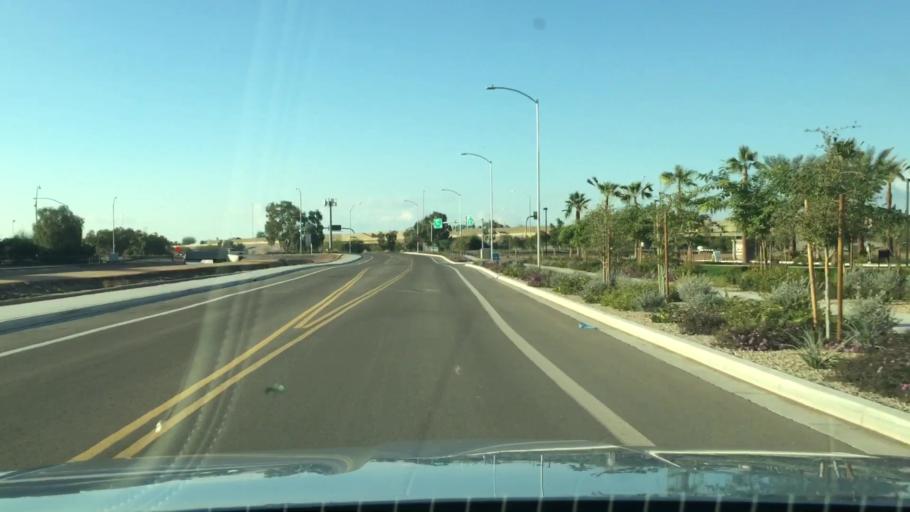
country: US
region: Arizona
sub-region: Maricopa County
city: Gilbert
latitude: 33.3836
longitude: -111.7354
